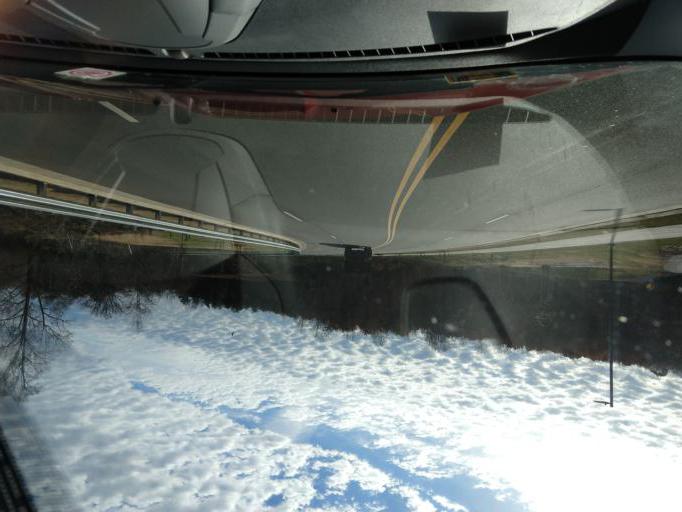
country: US
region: Virginia
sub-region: City of Lynchburg
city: West Lynchburg
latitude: 37.3401
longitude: -79.1854
